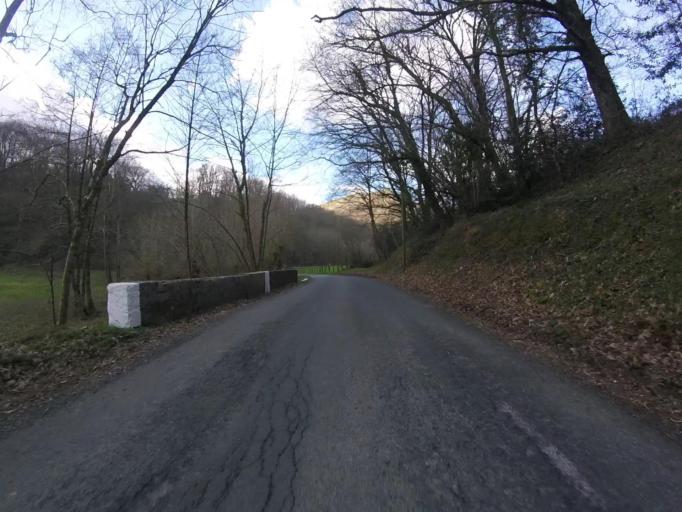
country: FR
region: Aquitaine
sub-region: Departement des Pyrenees-Atlantiques
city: Sare
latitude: 43.2800
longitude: -1.5952
